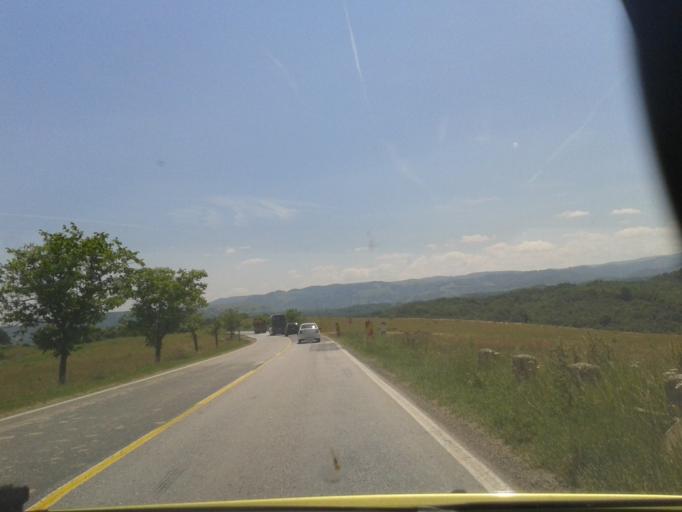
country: RO
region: Timis
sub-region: Comuna Pietroasa
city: Pietroasa
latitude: 45.8851
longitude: 22.4145
